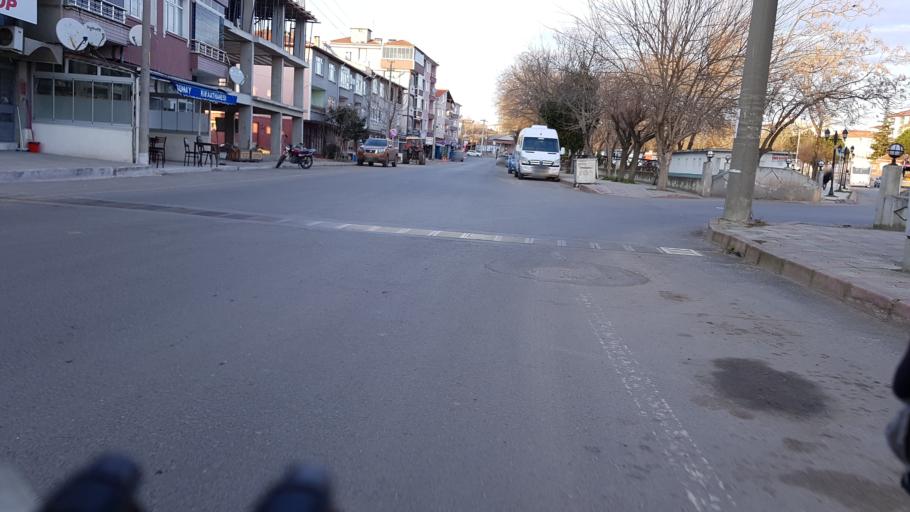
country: TR
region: Tekirdag
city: Velimese
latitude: 41.2531
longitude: 27.8767
